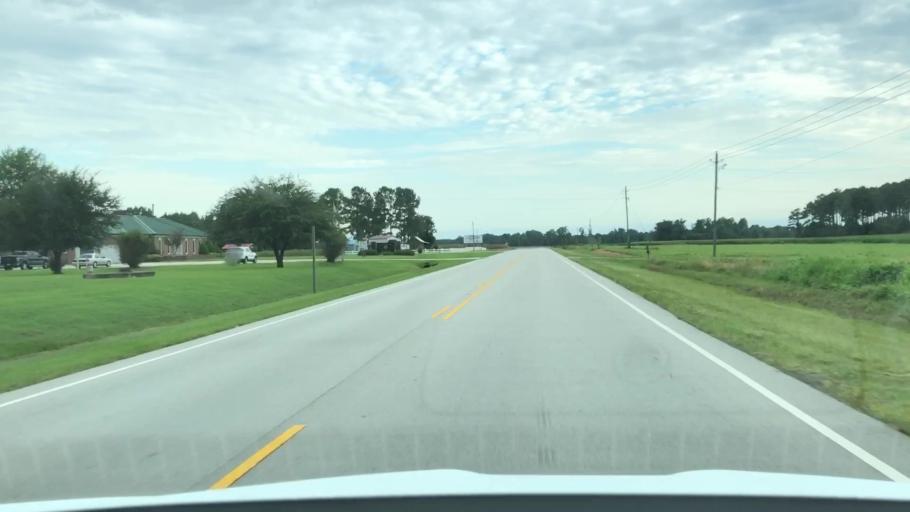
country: US
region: North Carolina
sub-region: Jones County
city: Trenton
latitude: 35.0443
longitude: -77.3513
